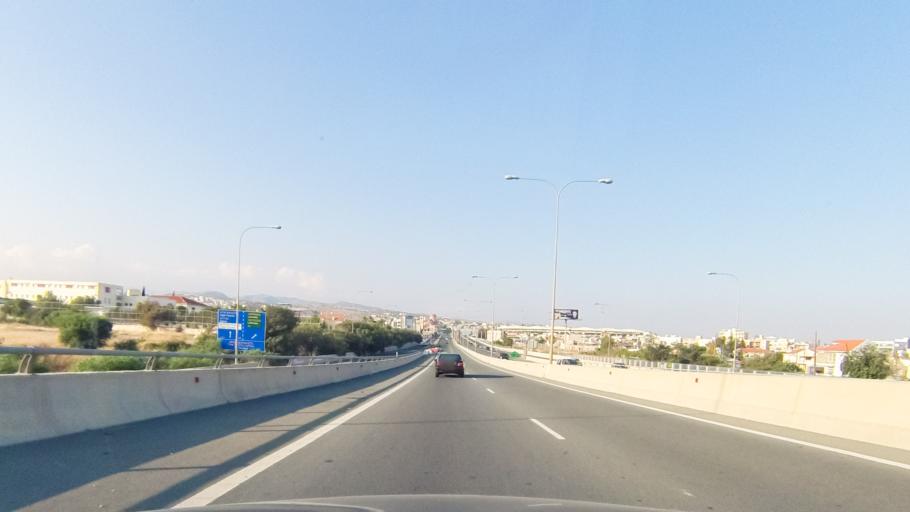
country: CY
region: Limassol
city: Pano Polemidia
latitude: 34.6962
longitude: 33.0156
